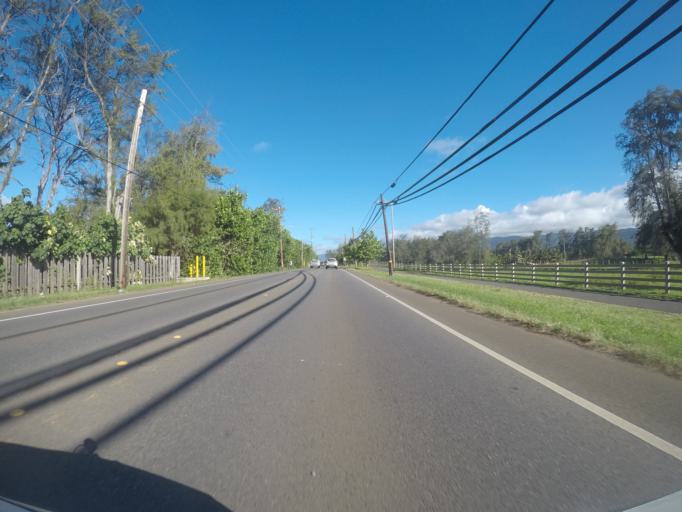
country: US
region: Hawaii
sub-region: Honolulu County
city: Kahuku
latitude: 21.6659
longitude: -157.9372
